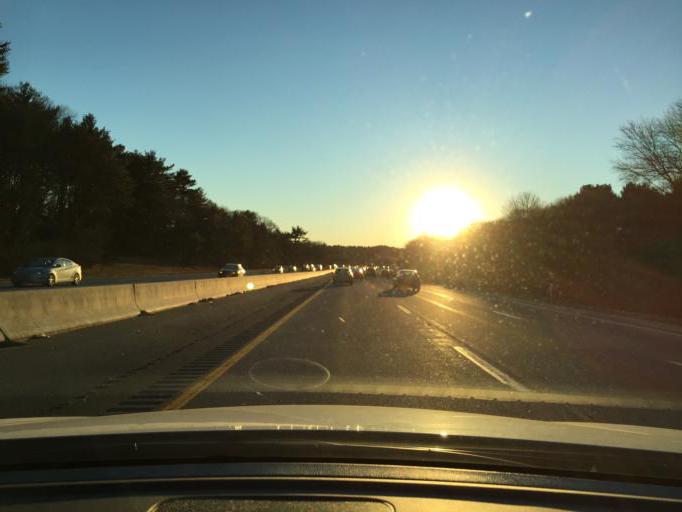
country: US
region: Massachusetts
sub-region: Middlesex County
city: Cochituate
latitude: 42.3227
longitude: -71.3388
